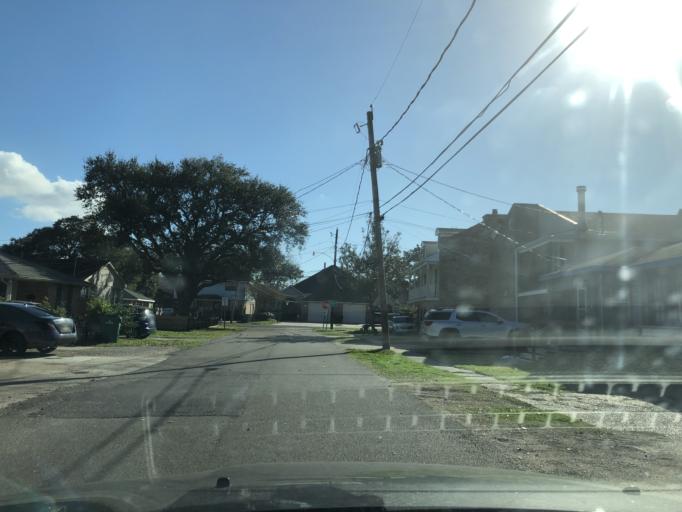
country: US
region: Louisiana
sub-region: Jefferson Parish
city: Metairie Terrace
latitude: 29.9808
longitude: -90.1652
